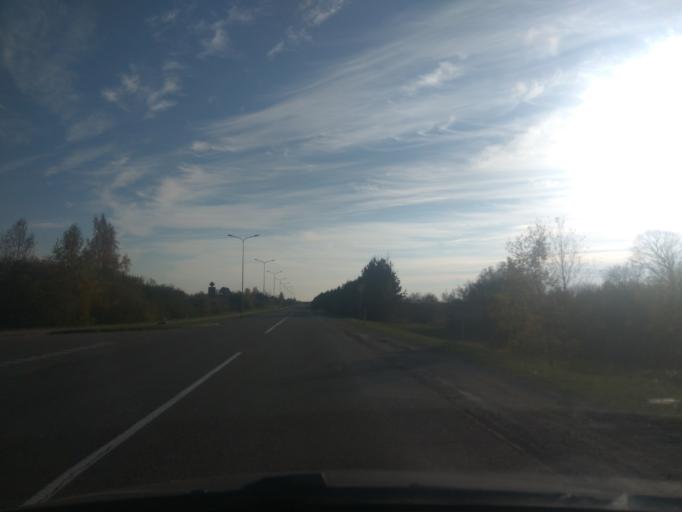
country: LV
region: Ventspils
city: Ventspils
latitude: 57.3586
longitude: 21.5634
